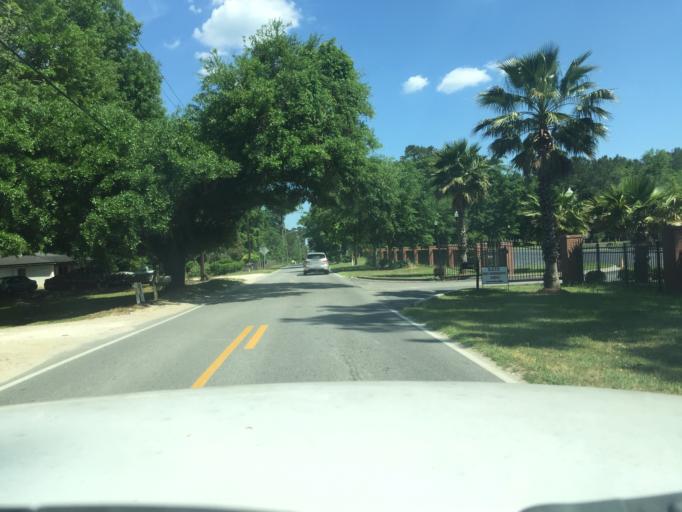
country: US
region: Georgia
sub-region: Chatham County
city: Georgetown
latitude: 32.0020
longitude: -81.2796
